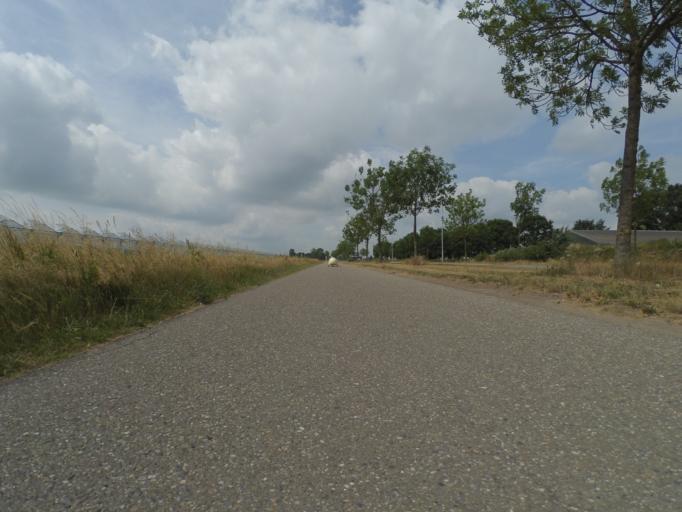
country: NL
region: North Brabant
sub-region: Gemeente Made en Drimmelen
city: Drimmelen
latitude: 51.6920
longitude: 4.8165
